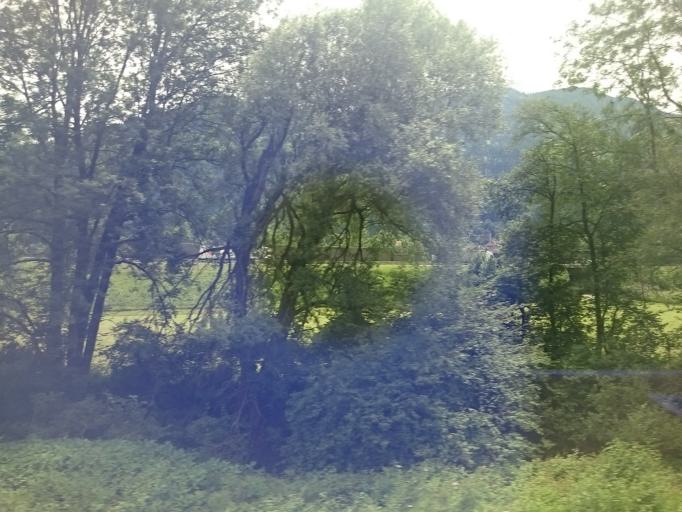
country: AT
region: Tyrol
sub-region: Politischer Bezirk Schwaz
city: Wiesing
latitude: 47.3938
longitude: 11.7938
